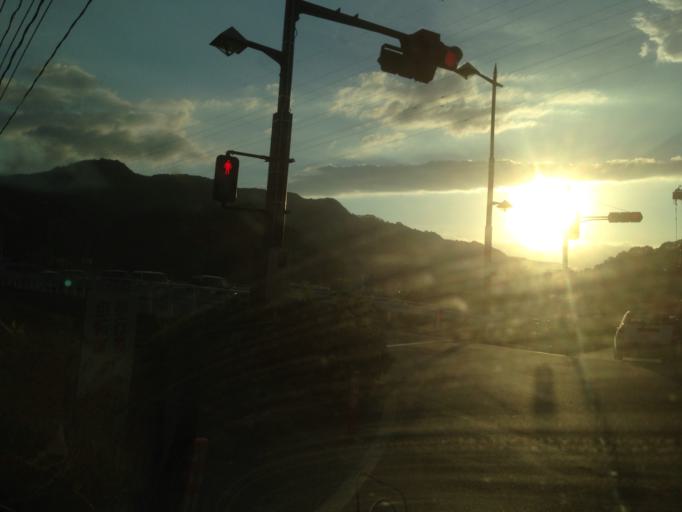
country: JP
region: Iwate
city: Otsuchi
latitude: 39.3565
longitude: 141.8955
